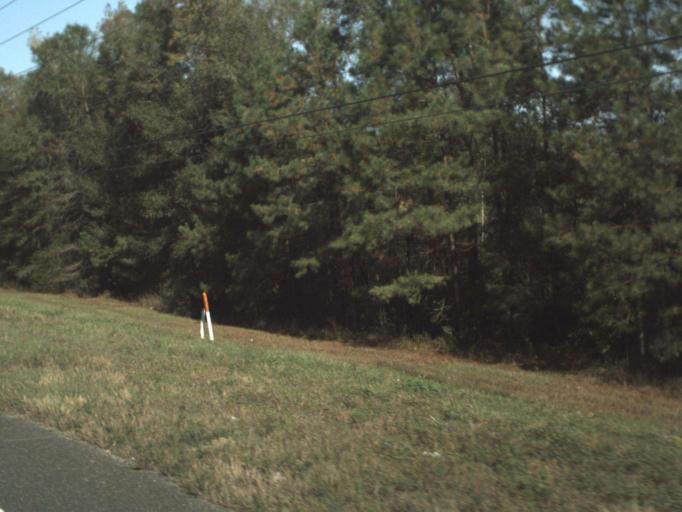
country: US
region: Florida
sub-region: Gadsden County
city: Midway
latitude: 30.4767
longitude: -84.4114
